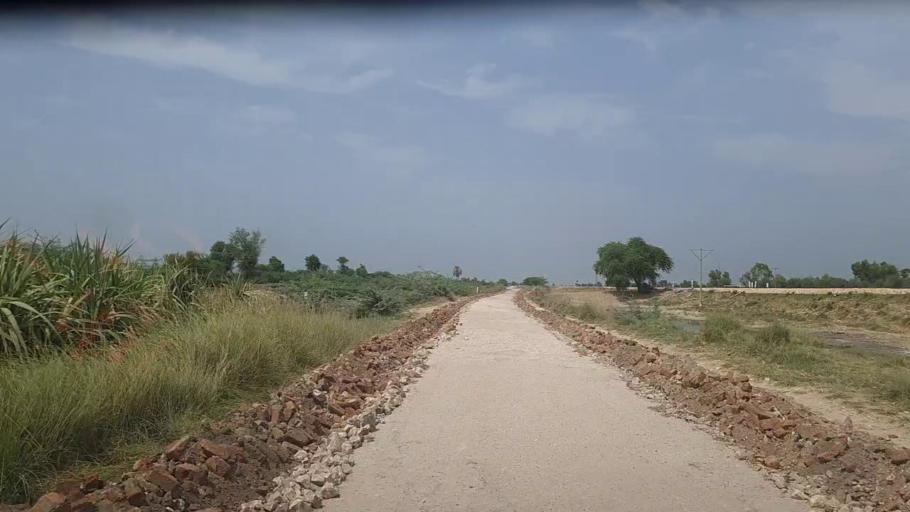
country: PK
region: Sindh
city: Bhiria
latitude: 26.9090
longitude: 68.2921
